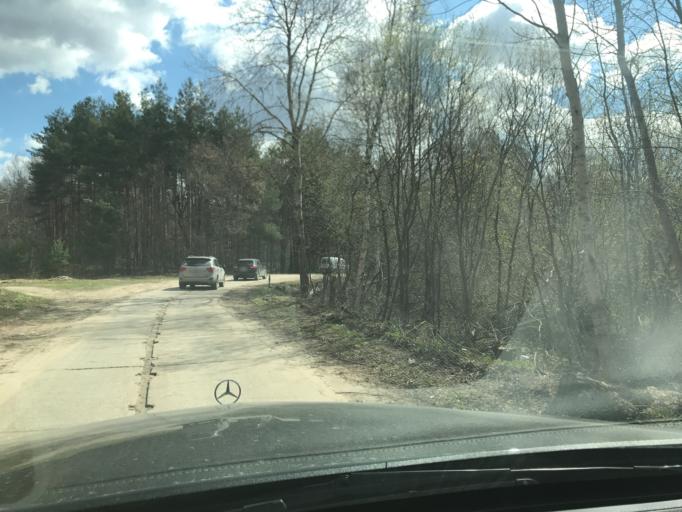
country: RU
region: Moskovskaya
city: Vereya
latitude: 55.8391
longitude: 39.0828
